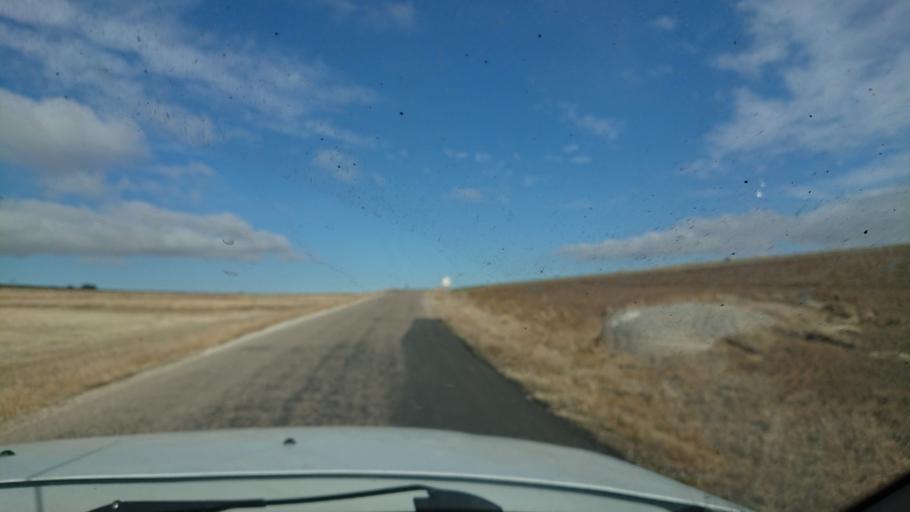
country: TR
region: Aksaray
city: Agacoren
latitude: 38.8365
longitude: 33.9541
